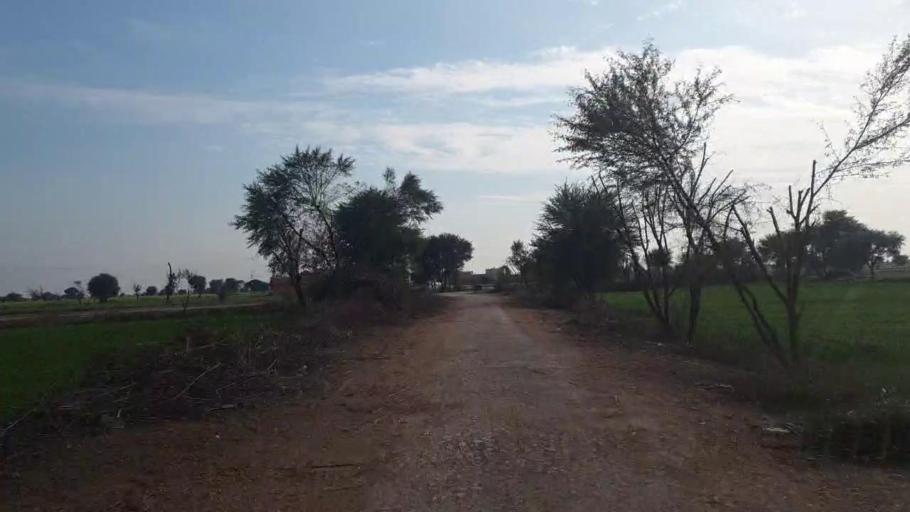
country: PK
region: Sindh
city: Shahdadpur
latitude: 26.0482
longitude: 68.5644
